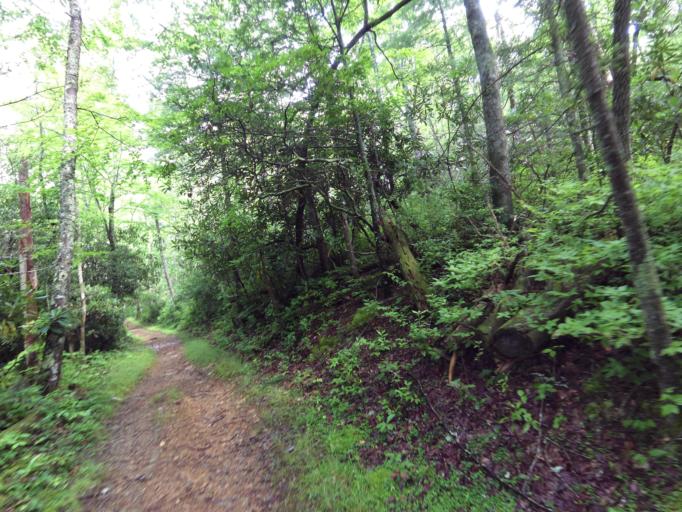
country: US
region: Tennessee
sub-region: Blount County
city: Wildwood
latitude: 35.6029
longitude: -83.7650
